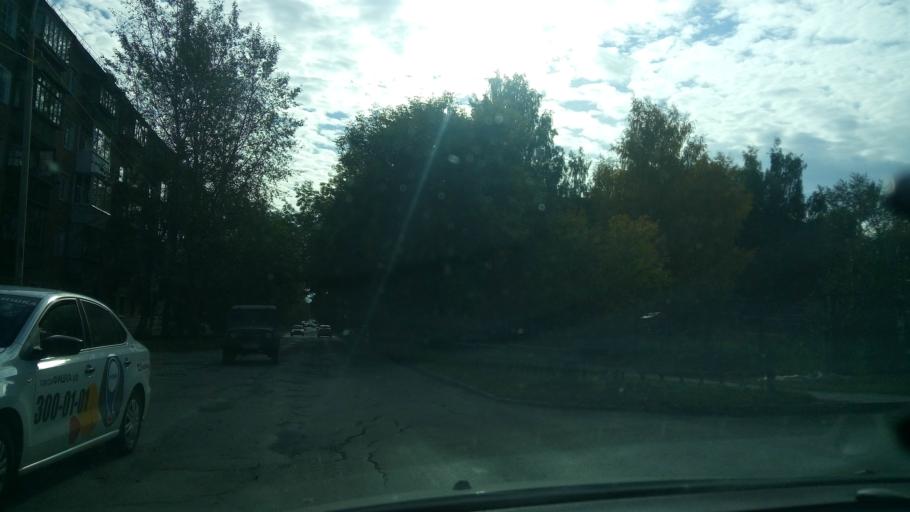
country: RU
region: Sverdlovsk
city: Yekaterinburg
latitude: 56.9018
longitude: 60.6018
